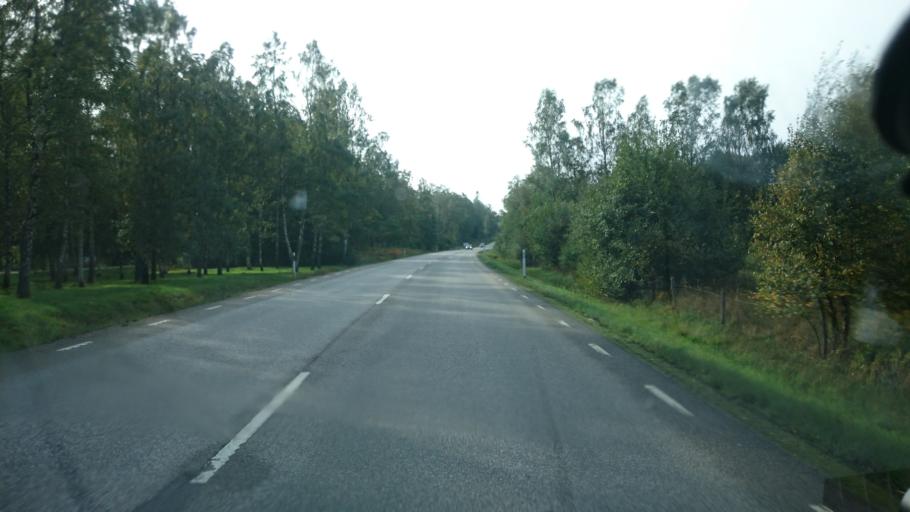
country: SE
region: Vaestra Goetaland
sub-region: Alingsas Kommun
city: Sollebrunn
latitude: 58.0813
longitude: 12.4875
